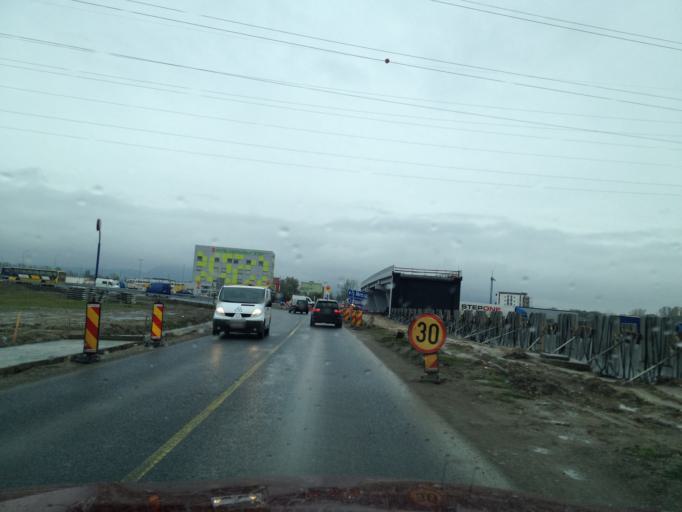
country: RO
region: Brasov
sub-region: Comuna Sanpetru
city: Sanpetru
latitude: 45.6905
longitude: 25.6212
